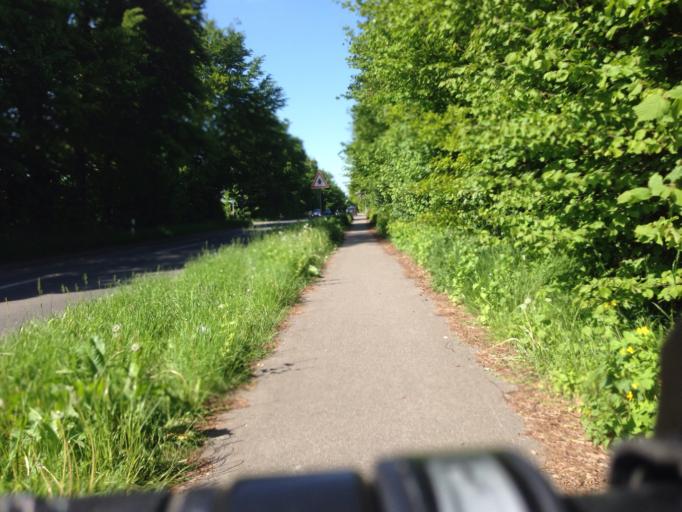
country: DE
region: Schleswig-Holstein
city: Stapelfeld
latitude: 53.6111
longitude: 10.2215
